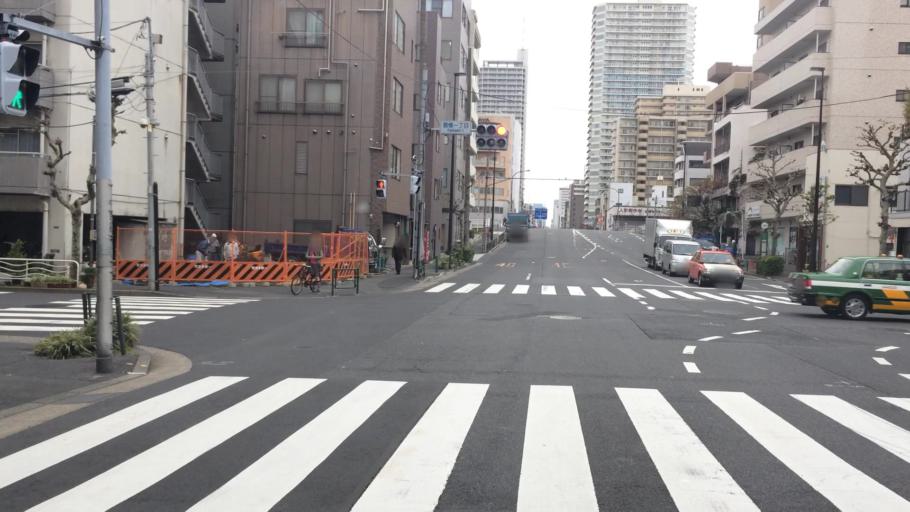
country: JP
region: Tokyo
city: Urayasu
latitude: 35.6828
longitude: 139.8116
